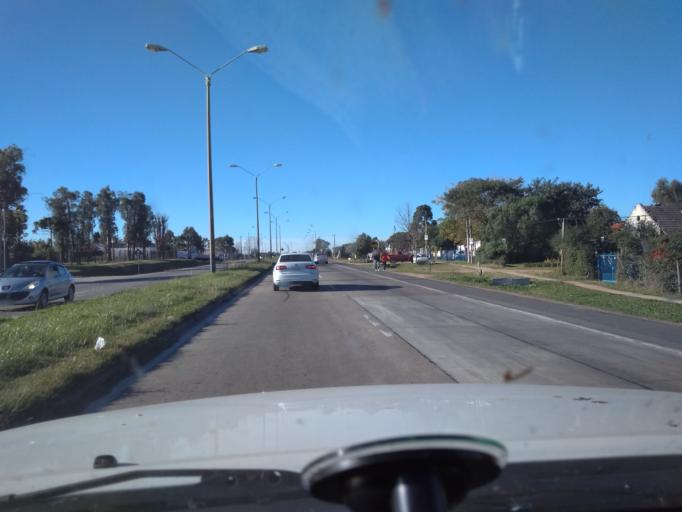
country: UY
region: Canelones
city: Colonia Nicolich
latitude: -34.7802
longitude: -56.0587
